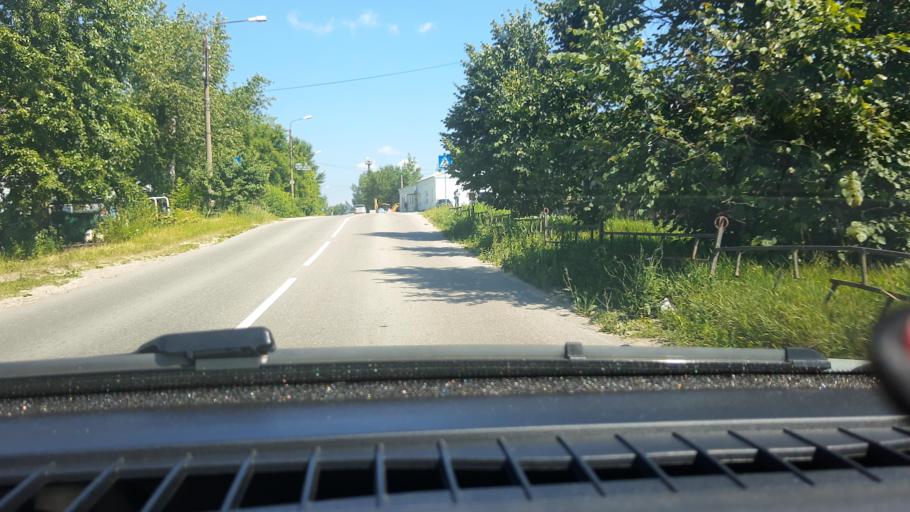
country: RU
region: Nizjnij Novgorod
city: Afonino
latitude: 56.2878
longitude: 44.1911
